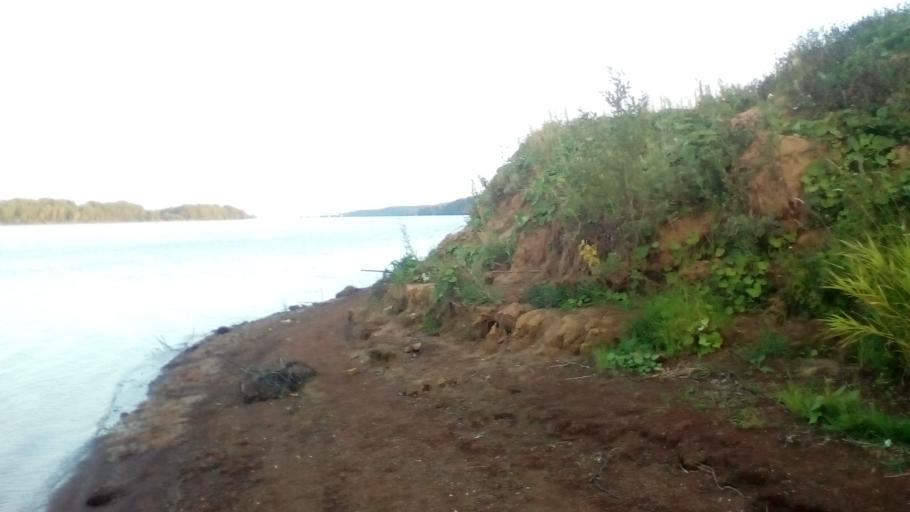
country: RU
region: Perm
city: Usol'ye
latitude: 59.4867
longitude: 56.5875
